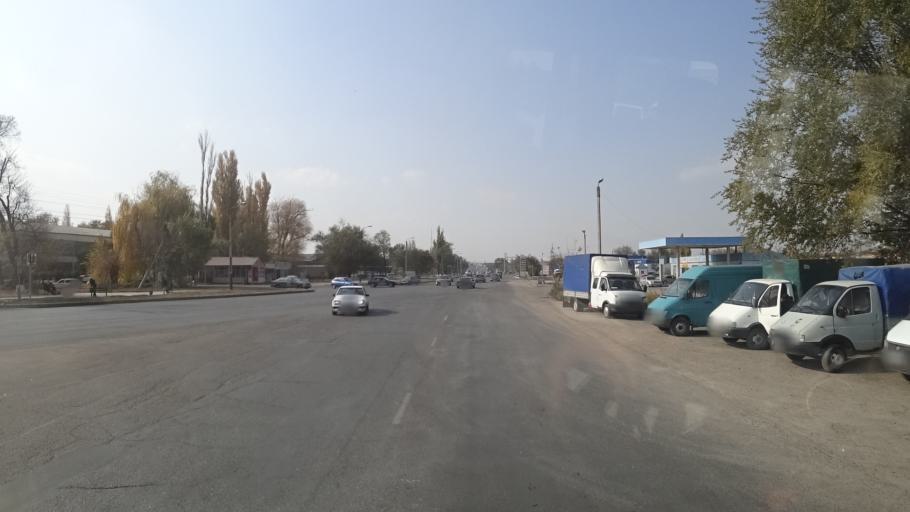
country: KZ
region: Zhambyl
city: Taraz
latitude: 42.9233
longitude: 71.4188
